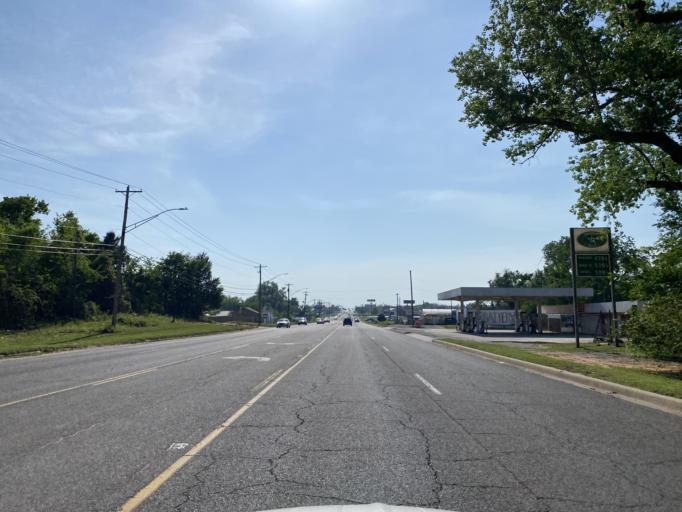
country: US
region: Oklahoma
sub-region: Oklahoma County
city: Spencer
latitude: 35.4931
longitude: -97.3631
